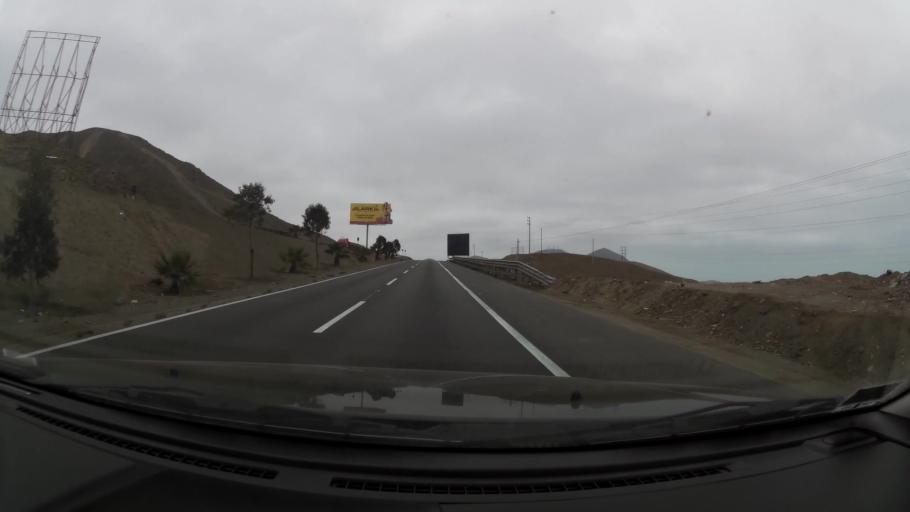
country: PE
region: Lima
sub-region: Lima
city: San Bartolo
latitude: -12.4334
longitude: -76.7544
